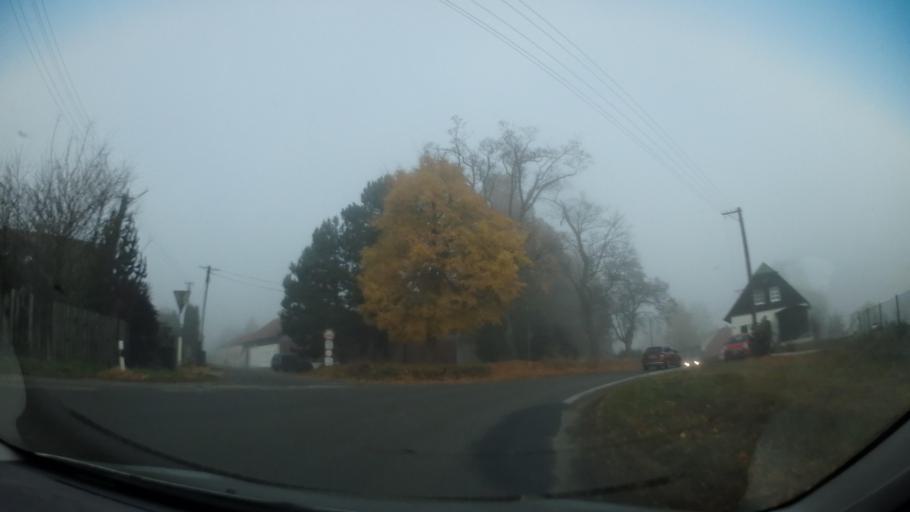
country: CZ
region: Vysocina
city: Krizanov
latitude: 49.4698
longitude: 16.0896
